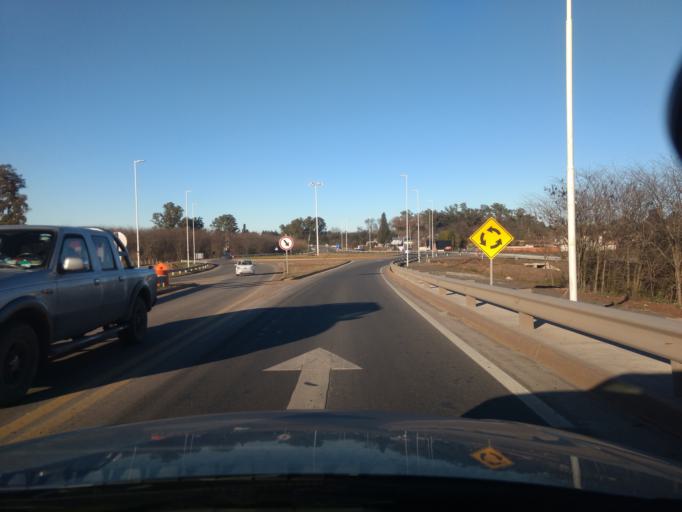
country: AR
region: Buenos Aires
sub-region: Partido de Lujan
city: Lujan
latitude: -34.5911
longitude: -59.1045
